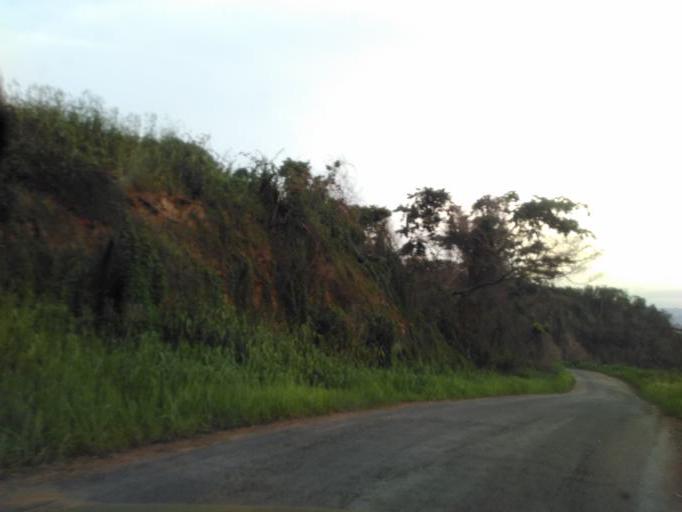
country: GH
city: Bekwai
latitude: 6.5527
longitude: -1.4275
